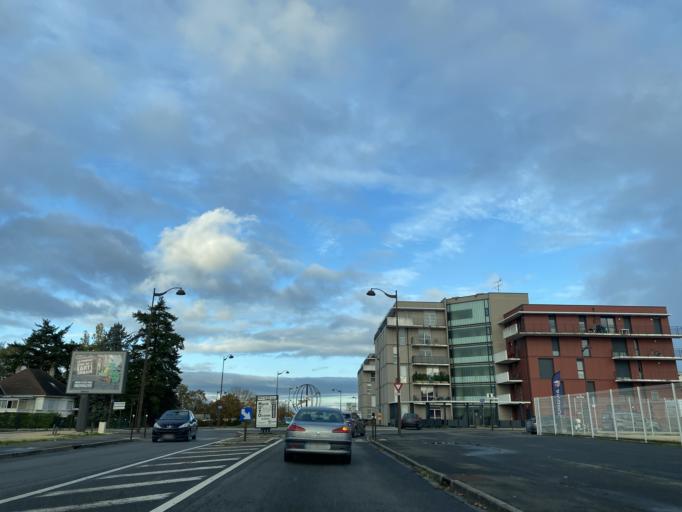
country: FR
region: Centre
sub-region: Departement du Cher
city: Bourges
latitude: 47.0682
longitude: 2.3740
